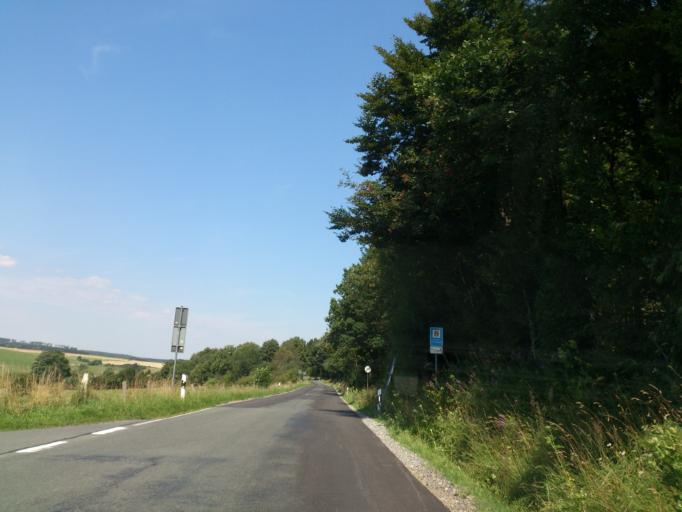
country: DE
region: North Rhine-Westphalia
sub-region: Regierungsbezirk Detmold
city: Altenbeken
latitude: 51.8004
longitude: 8.9506
